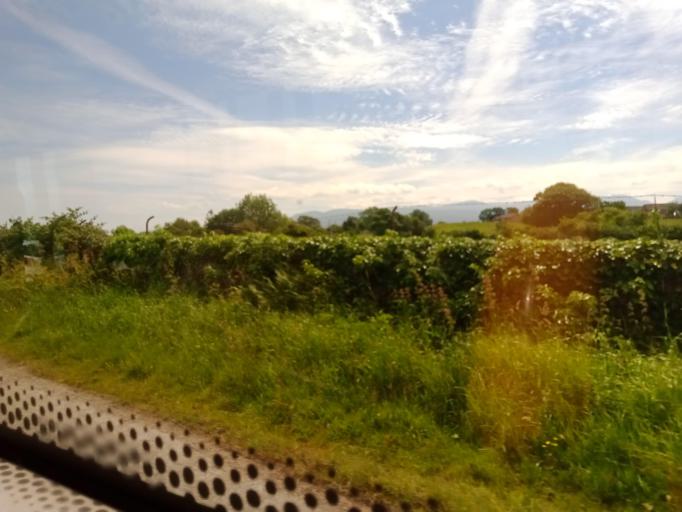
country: GB
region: Wales
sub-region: Gwynedd
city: Bangor
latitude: 53.2476
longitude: -4.1511
